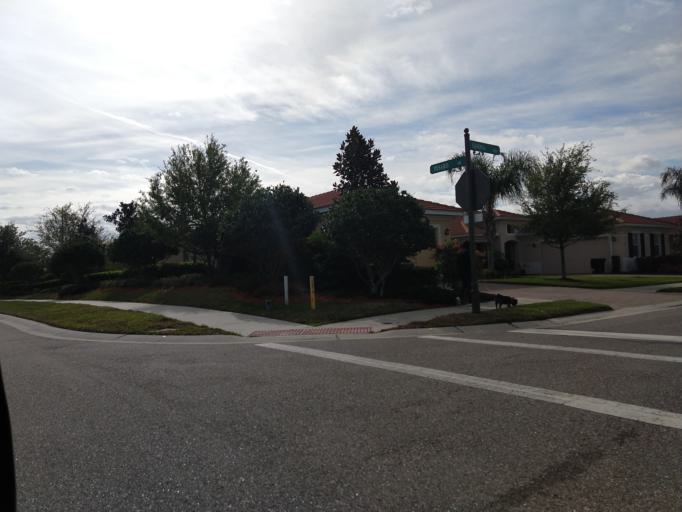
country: US
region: Florida
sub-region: Sarasota County
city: Plantation
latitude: 27.1392
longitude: -82.3741
